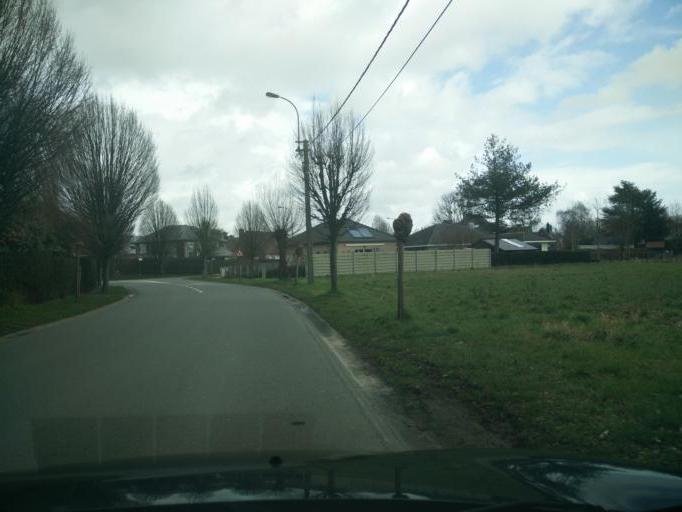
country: BE
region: Flanders
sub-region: Provincie Oost-Vlaanderen
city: Melle
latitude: 51.0308
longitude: 3.8131
